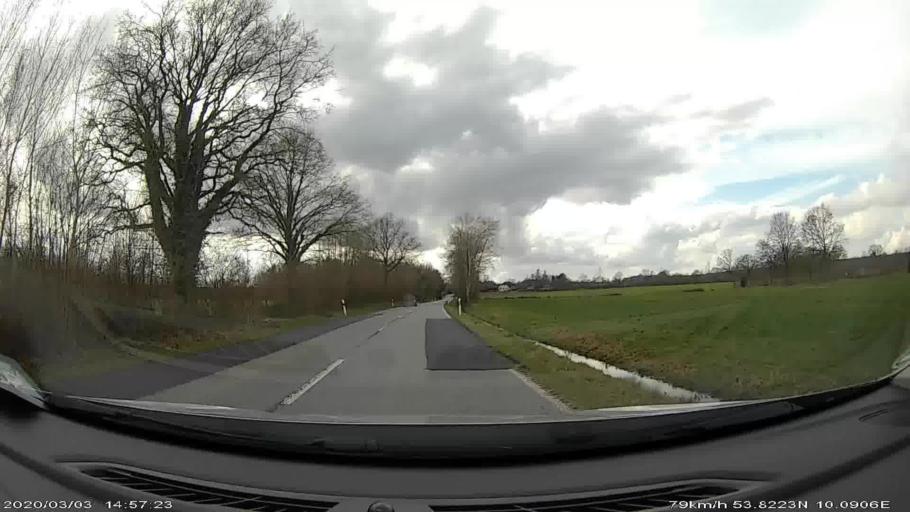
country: DE
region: Schleswig-Holstein
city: Huttblek
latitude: 53.8225
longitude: 10.0911
